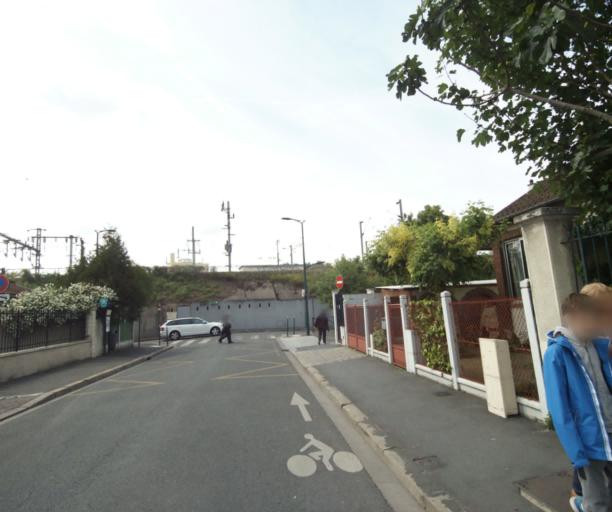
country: FR
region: Ile-de-France
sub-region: Departement des Hauts-de-Seine
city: Colombes
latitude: 48.9305
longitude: 2.2611
